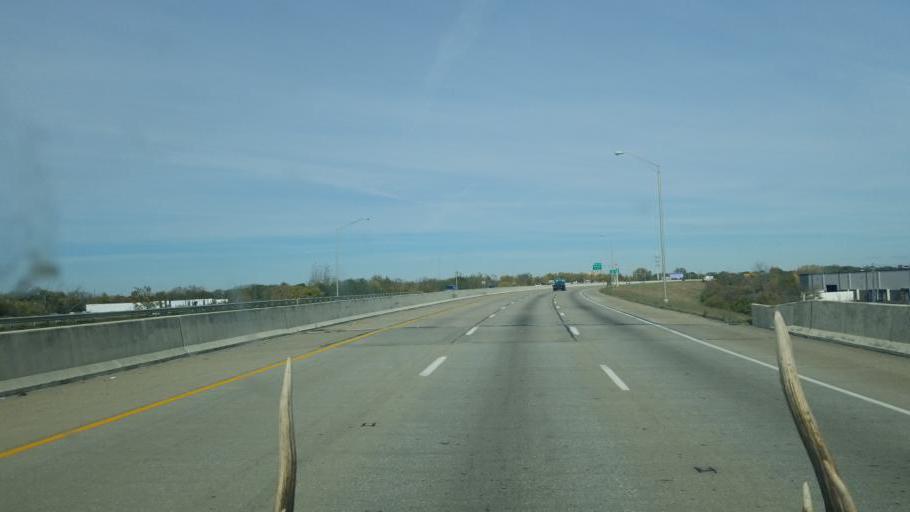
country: US
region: Indiana
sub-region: Marion County
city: Speedway
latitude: 39.7425
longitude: -86.2383
